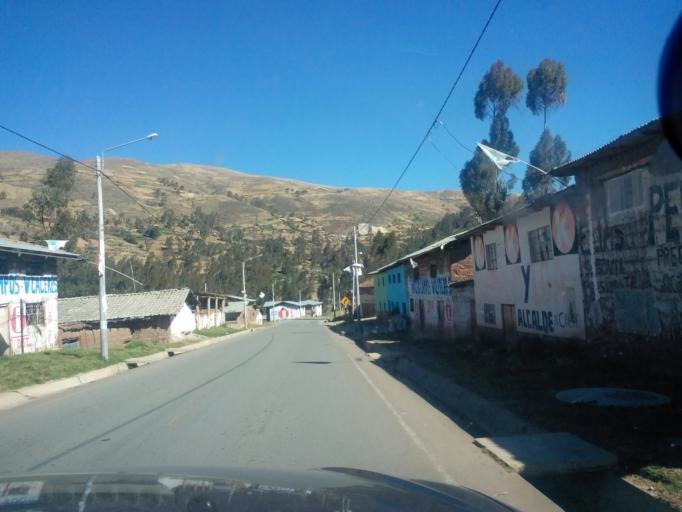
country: PE
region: Apurimac
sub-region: Provincia de Andahuaylas
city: Talavera
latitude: -13.6518
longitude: -73.5164
